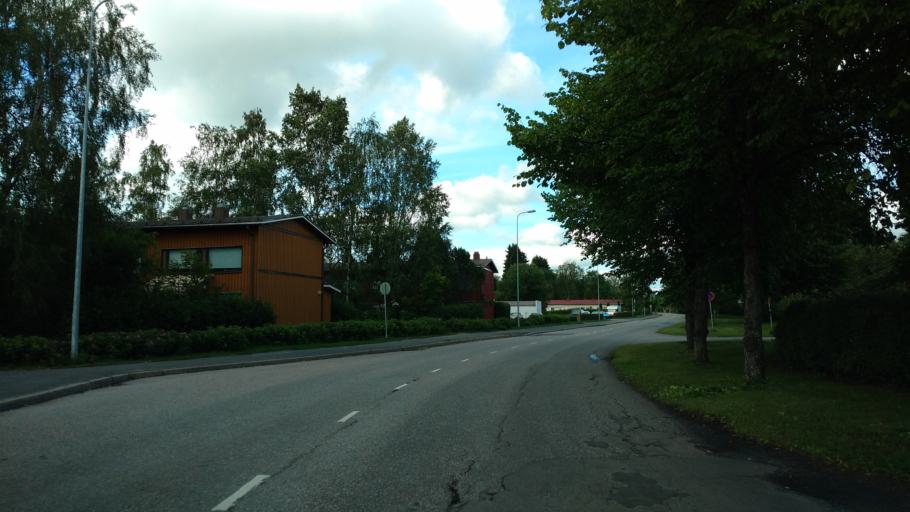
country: FI
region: Varsinais-Suomi
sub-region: Salo
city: Salo
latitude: 60.3969
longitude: 23.1402
